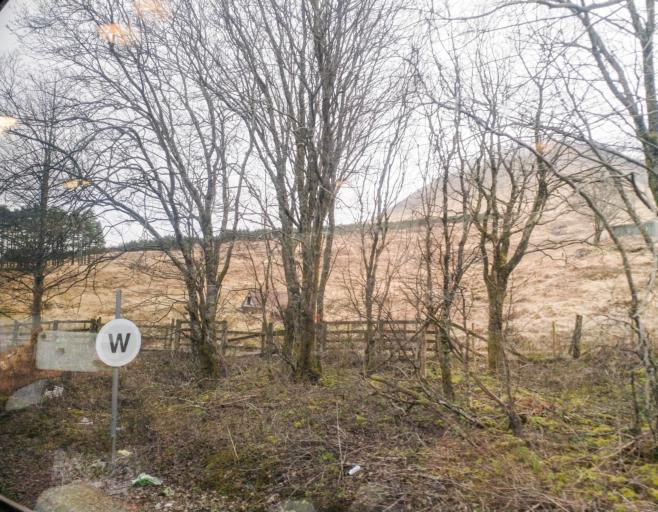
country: GB
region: Scotland
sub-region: Highland
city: Spean Bridge
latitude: 56.5170
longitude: -4.7644
